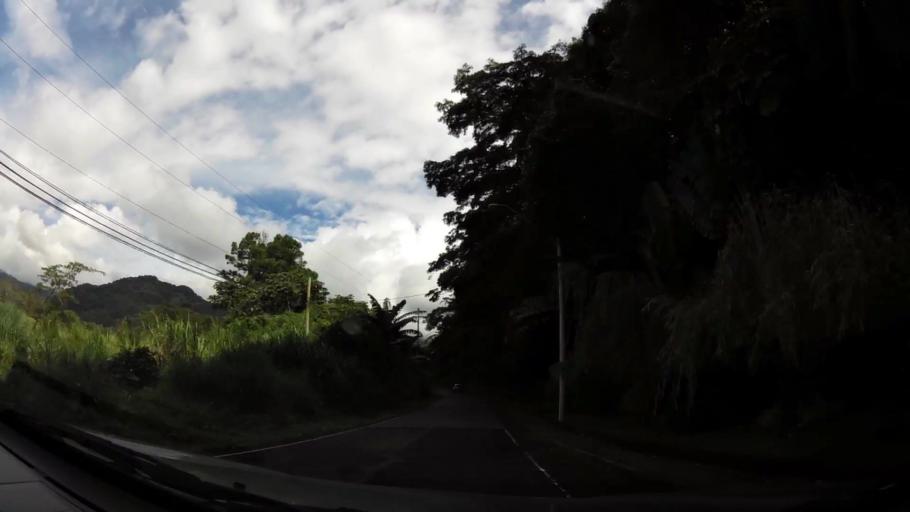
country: PA
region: Chiriqui
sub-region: Distrito Boquete
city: Boquete
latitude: 8.7856
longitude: -82.4288
